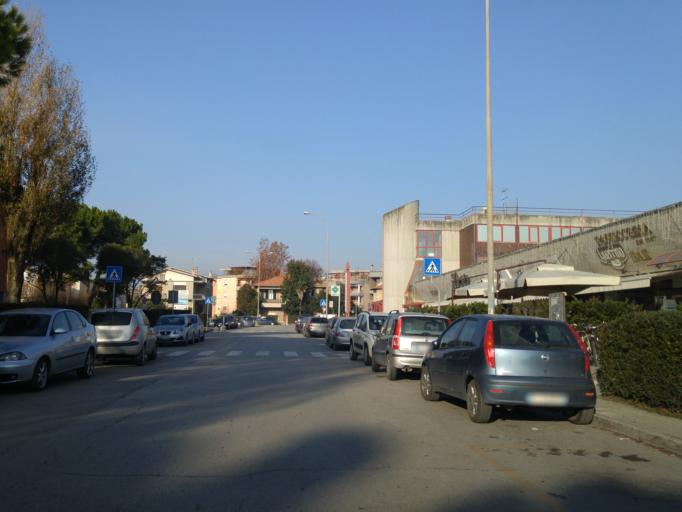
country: IT
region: The Marches
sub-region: Provincia di Pesaro e Urbino
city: Fano
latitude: 43.8335
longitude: 13.0047
